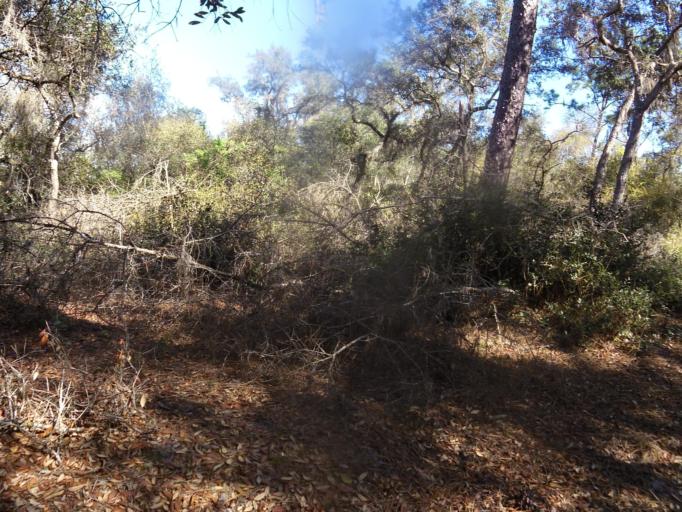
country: US
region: Florida
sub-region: Clay County
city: Keystone Heights
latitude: 29.8374
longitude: -82.0037
